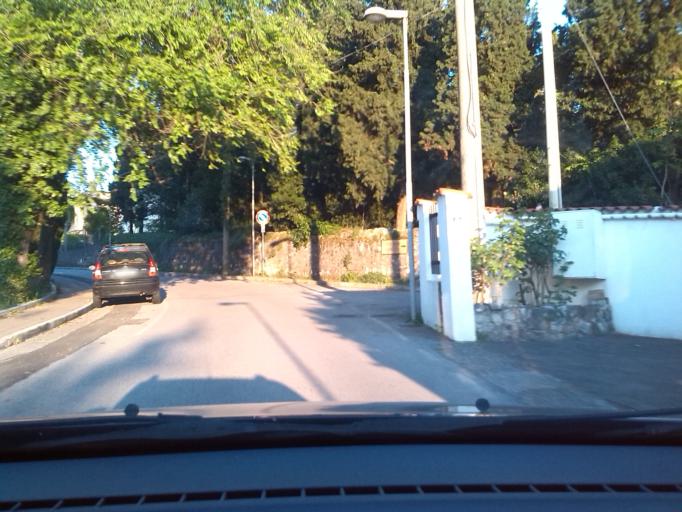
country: IT
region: Friuli Venezia Giulia
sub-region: Provincia di Trieste
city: Duino
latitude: 45.7733
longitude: 13.6015
